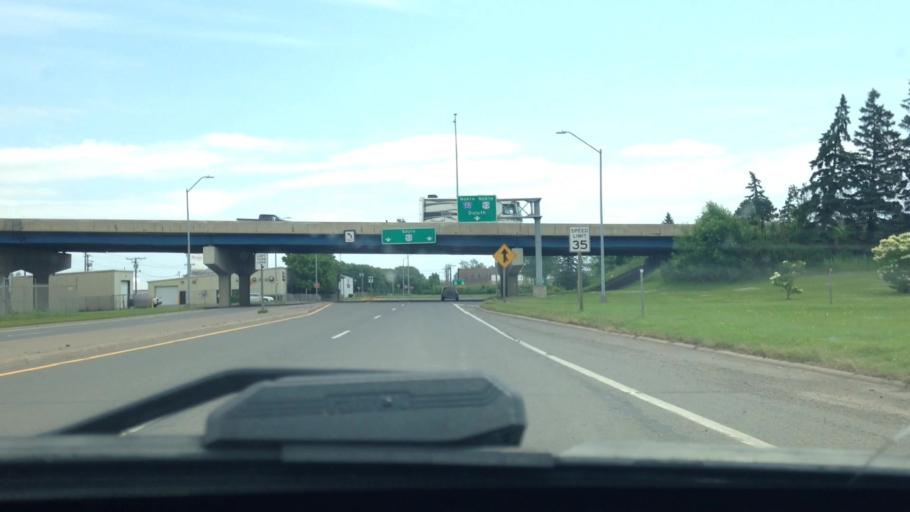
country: US
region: Wisconsin
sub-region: Douglas County
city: Superior
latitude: 46.7351
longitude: -92.0989
